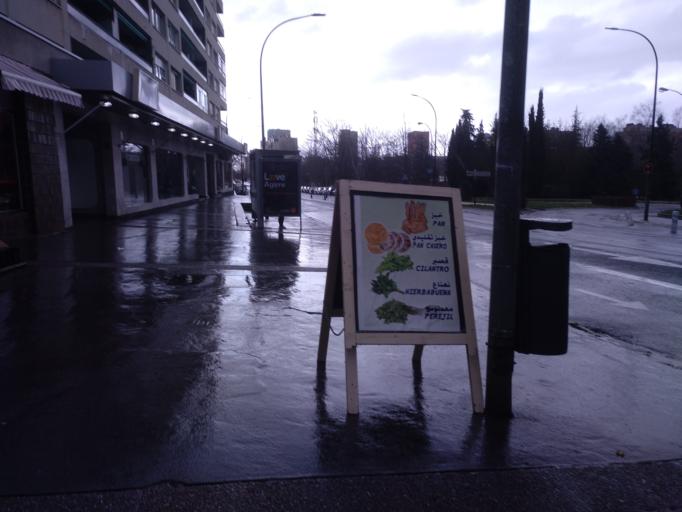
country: ES
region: Basque Country
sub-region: Provincia de Alava
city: Gasteiz / Vitoria
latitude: 42.8479
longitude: -2.6593
